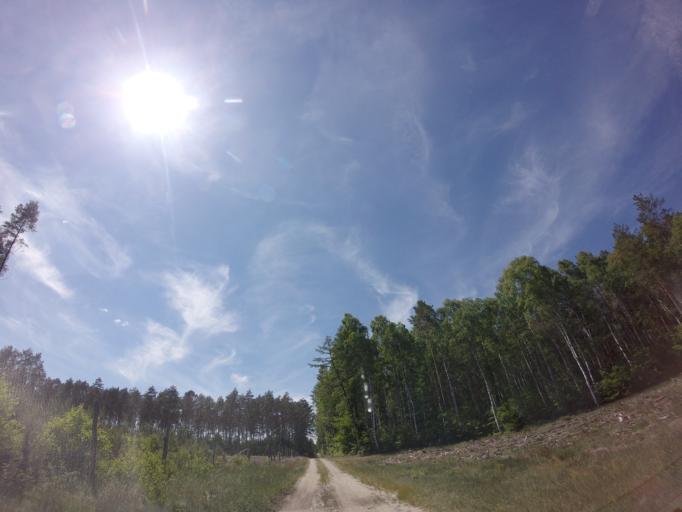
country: PL
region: West Pomeranian Voivodeship
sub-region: Powiat drawski
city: Kalisz Pomorski
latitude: 53.1642
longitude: 15.8920
